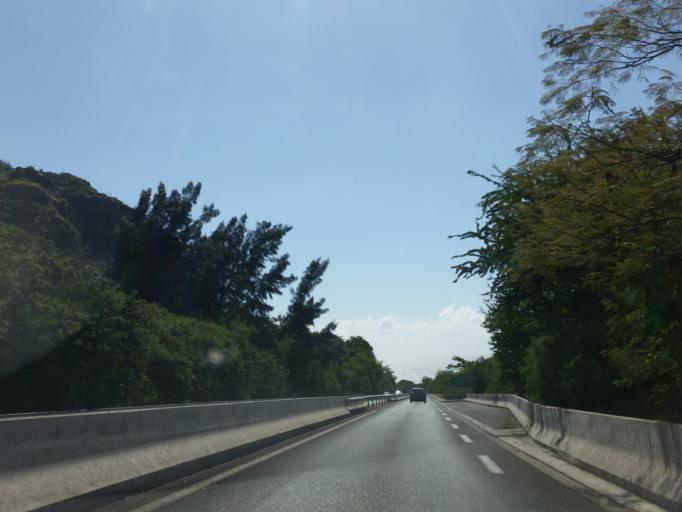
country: RE
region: Reunion
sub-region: Reunion
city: Saint-Denis
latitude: -20.8835
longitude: 55.4392
